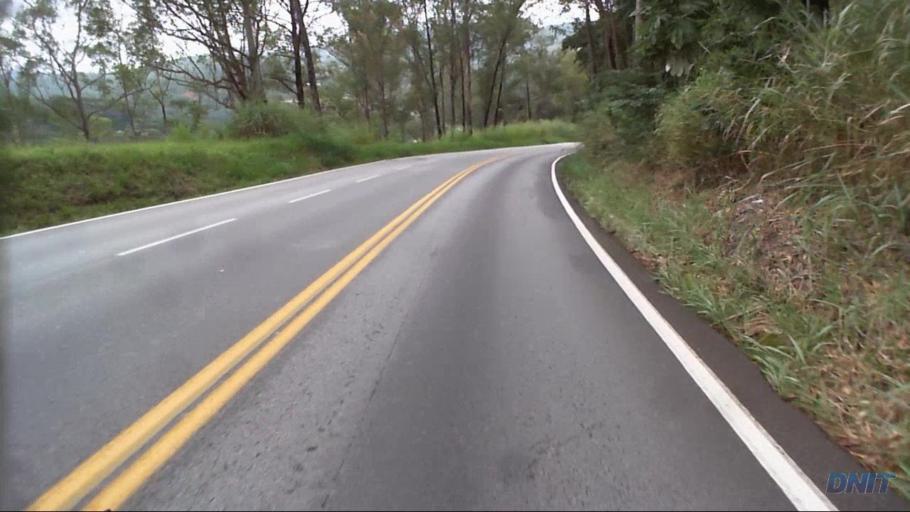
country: BR
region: Minas Gerais
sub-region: Joao Monlevade
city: Joao Monlevade
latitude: -19.8601
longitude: -43.1102
